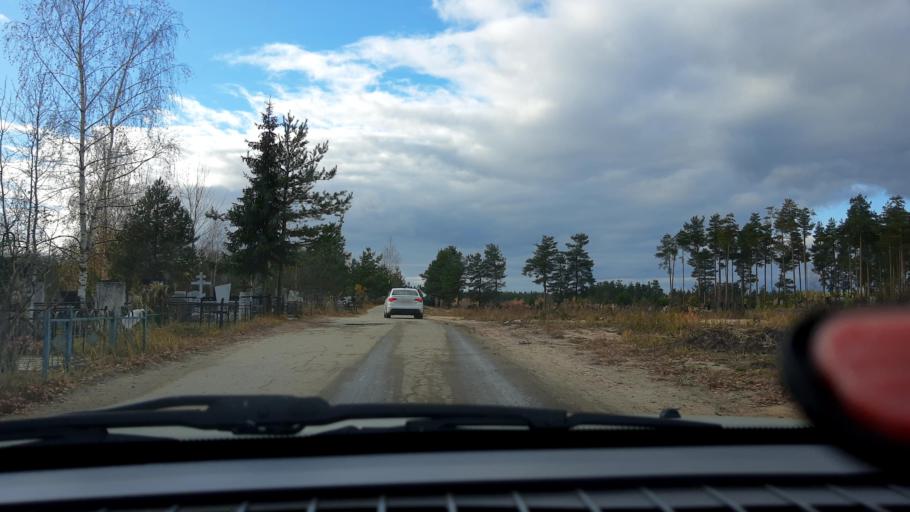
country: RU
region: Nizjnij Novgorod
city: Gorbatovka
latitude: 56.3601
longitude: 43.7728
